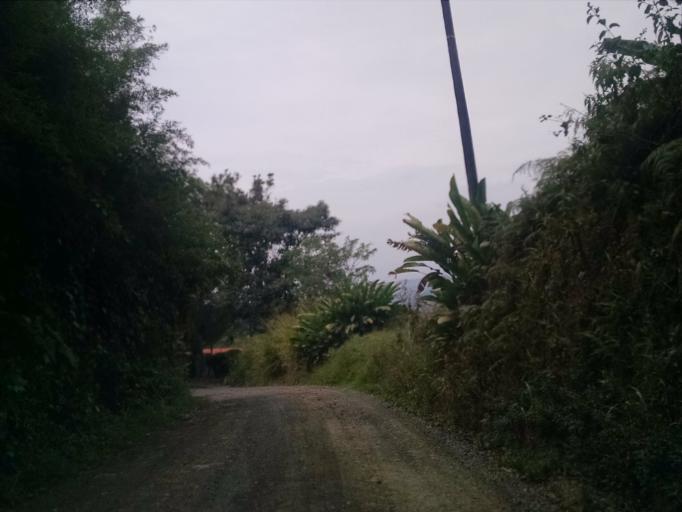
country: CO
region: Valle del Cauca
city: Ulloa
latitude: 4.7211
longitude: -75.7297
